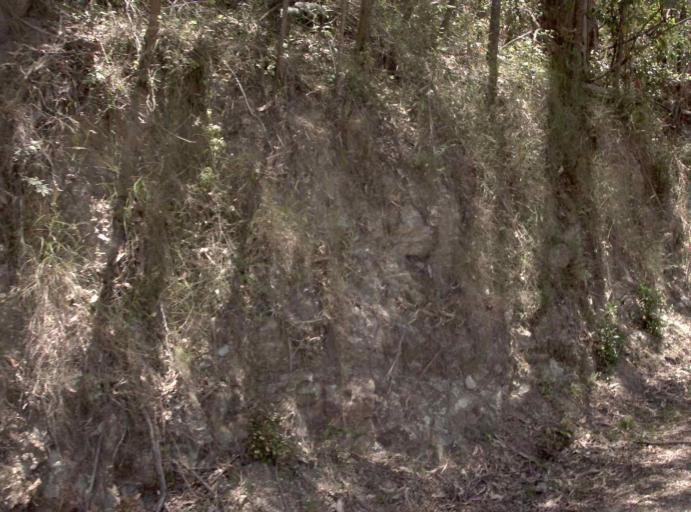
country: AU
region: New South Wales
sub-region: Bombala
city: Bombala
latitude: -37.4555
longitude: 148.9345
